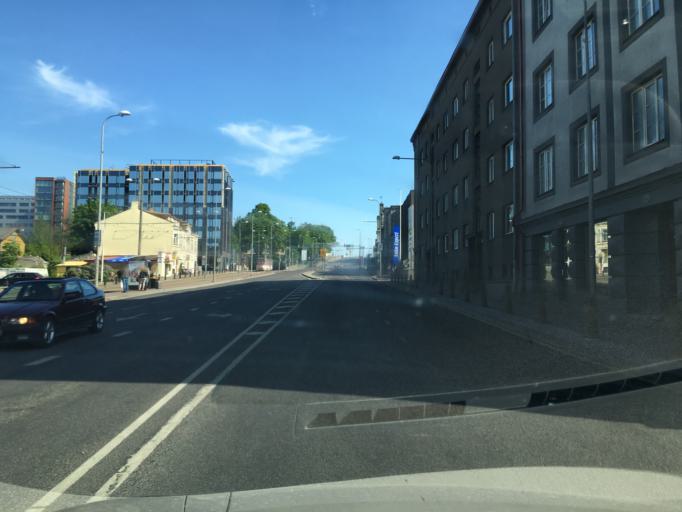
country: EE
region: Harju
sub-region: Tallinna linn
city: Tallinn
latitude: 59.4283
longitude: 24.7763
